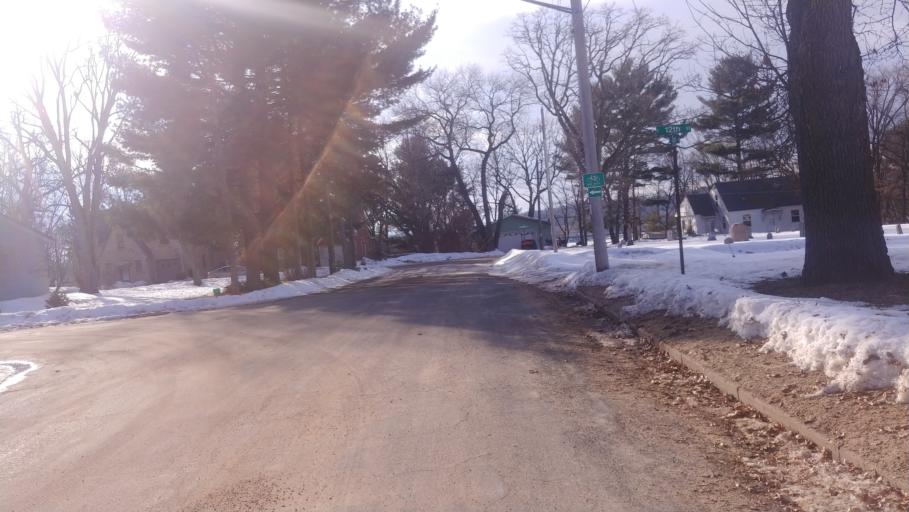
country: US
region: Wisconsin
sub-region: Dunn County
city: Menomonie
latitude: 44.8828
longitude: -91.9150
